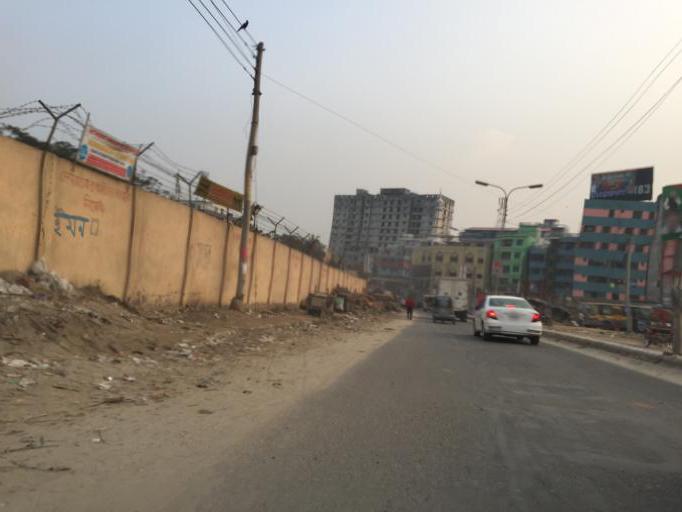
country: BD
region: Dhaka
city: Azimpur
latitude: 23.7966
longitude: 90.3474
